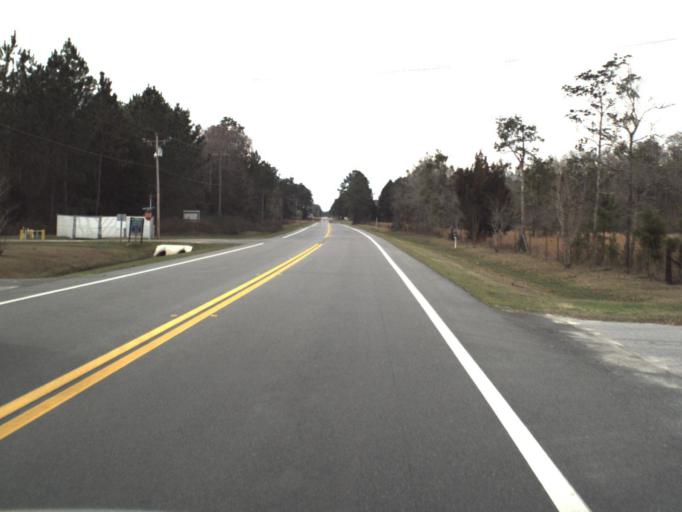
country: US
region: Florida
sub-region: Gulf County
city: Wewahitchka
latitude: 30.1185
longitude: -85.2101
